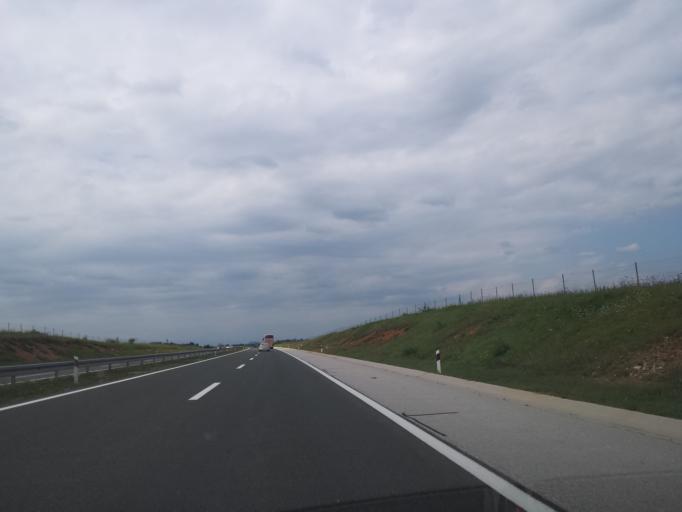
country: HR
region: Zadarska
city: Starigrad
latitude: 44.4685
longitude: 15.5938
